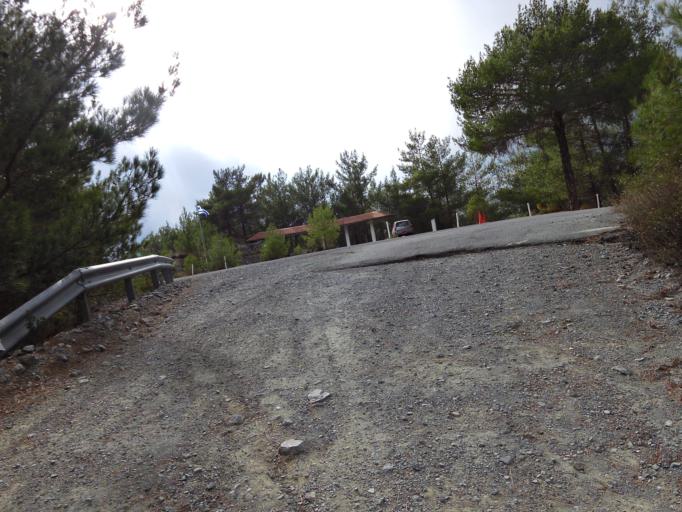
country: CY
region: Limassol
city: Pelendri
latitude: 34.9185
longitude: 32.9501
